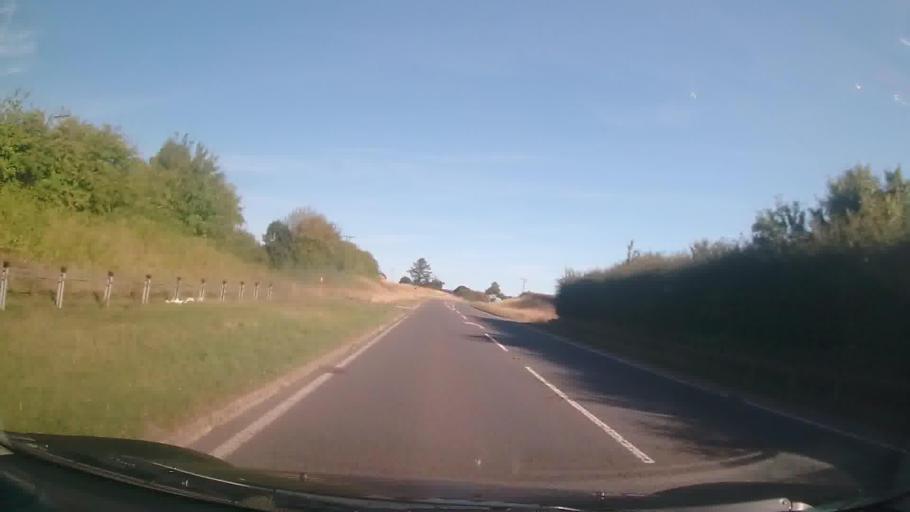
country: GB
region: Wales
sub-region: Sir Powys
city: Hay
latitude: 52.0071
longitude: -3.2435
